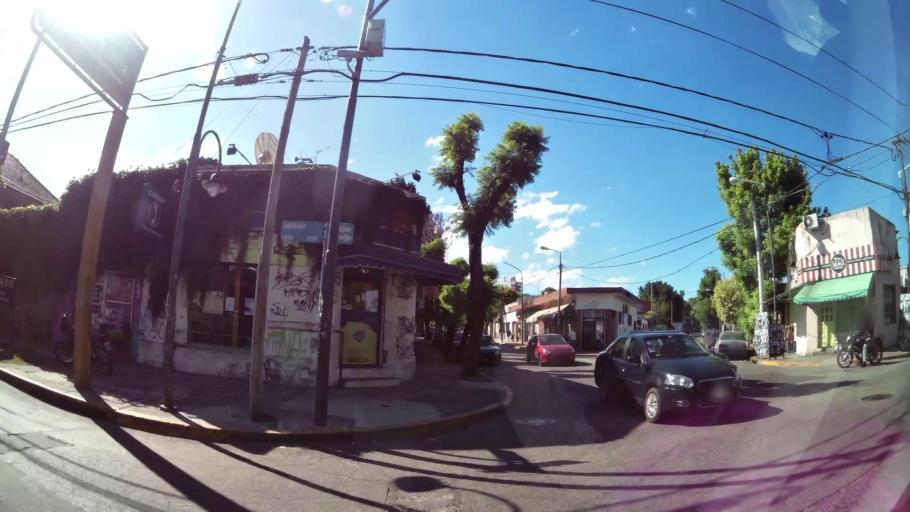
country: AR
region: Buenos Aires
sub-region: Partido de San Isidro
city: San Isidro
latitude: -34.4583
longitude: -58.5391
